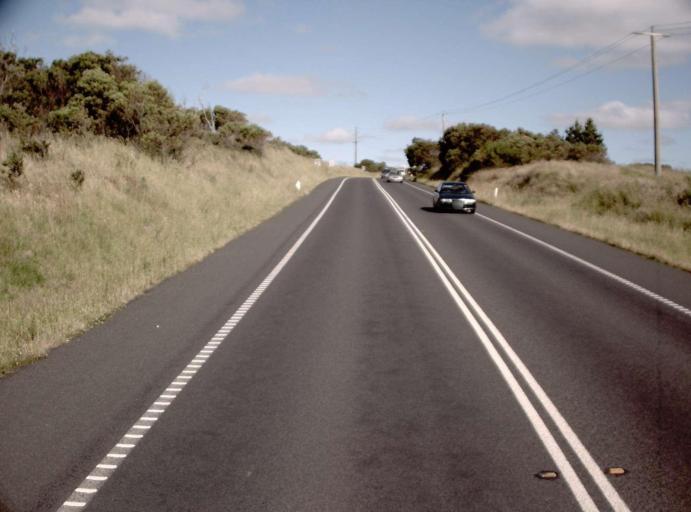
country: AU
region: Victoria
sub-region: Bass Coast
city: North Wonthaggi
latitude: -38.5317
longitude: 145.4503
